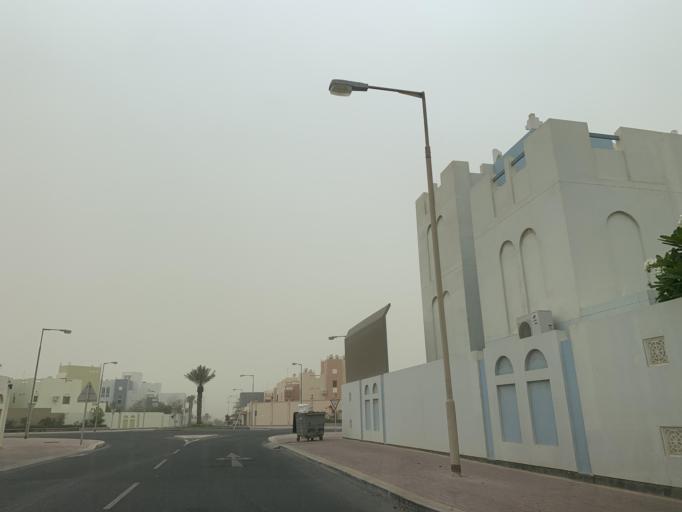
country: BH
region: Central Governorate
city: Madinat Hamad
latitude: 26.1320
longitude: 50.5121
